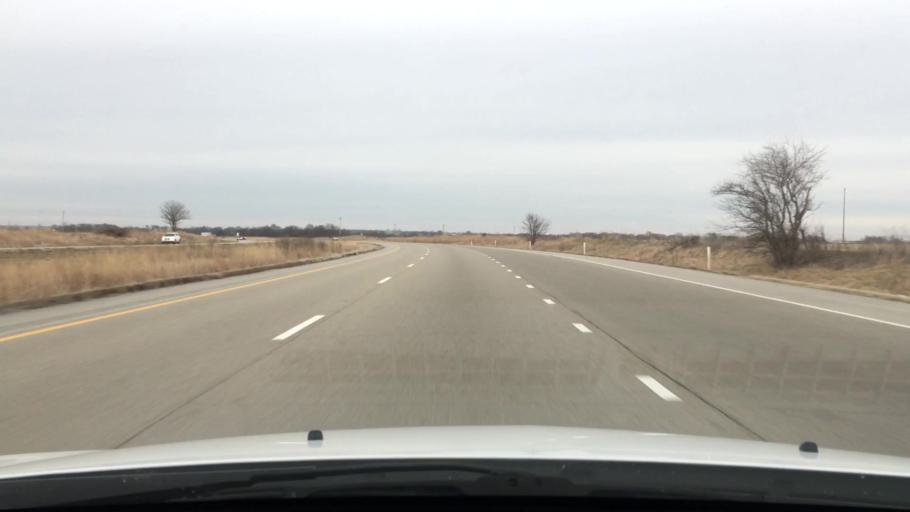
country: US
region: Illinois
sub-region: Logan County
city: Atlanta
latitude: 40.2633
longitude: -89.2160
